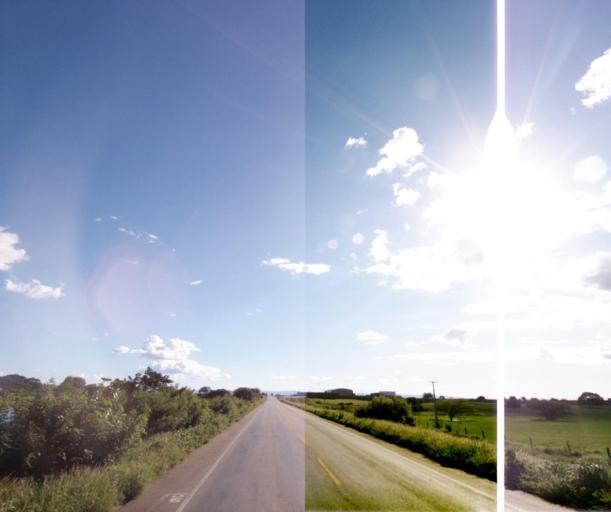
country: BR
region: Bahia
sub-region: Guanambi
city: Guanambi
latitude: -14.1743
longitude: -42.7286
